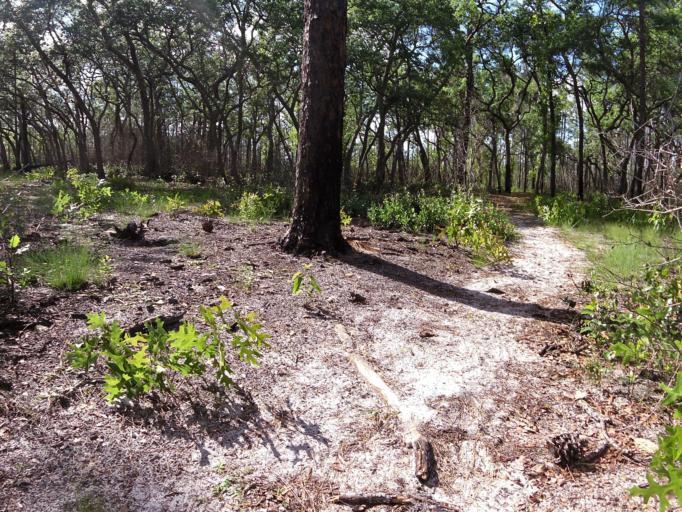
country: US
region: Florida
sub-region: Clay County
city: Keystone Heights
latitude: 29.8459
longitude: -81.9507
